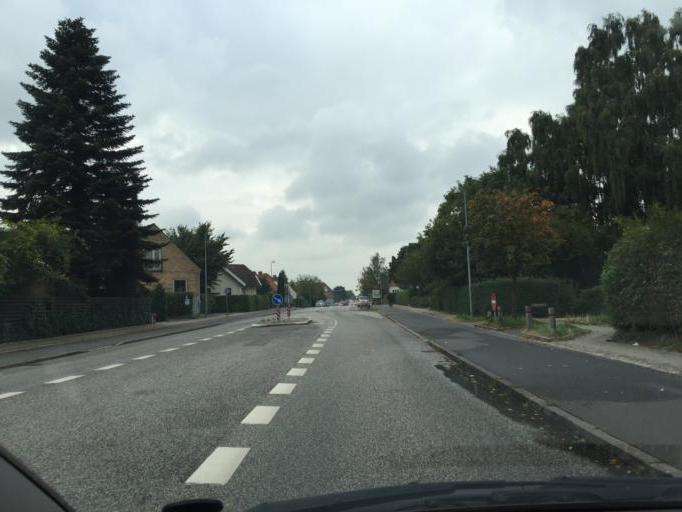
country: DK
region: Capital Region
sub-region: Gladsaxe Municipality
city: Buddinge
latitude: 55.7607
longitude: 12.4990
